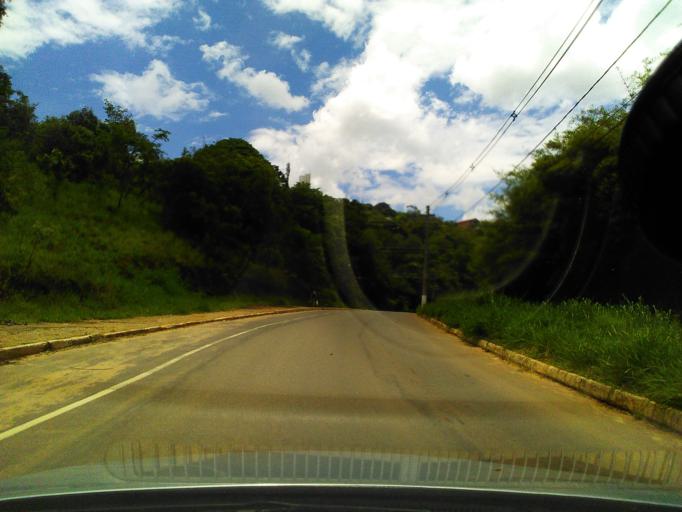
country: BR
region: Minas Gerais
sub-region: Tres Coracoes
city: Tres Coracoes
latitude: -21.7070
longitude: -45.2612
